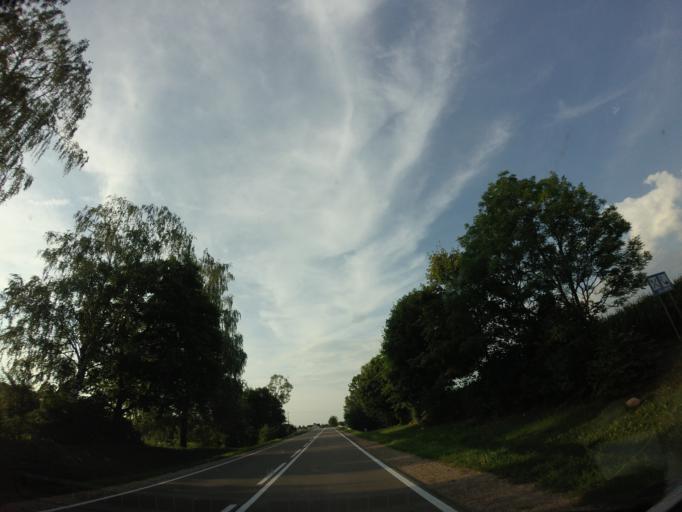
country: LT
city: Lazdijai
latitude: 54.1429
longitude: 23.4670
